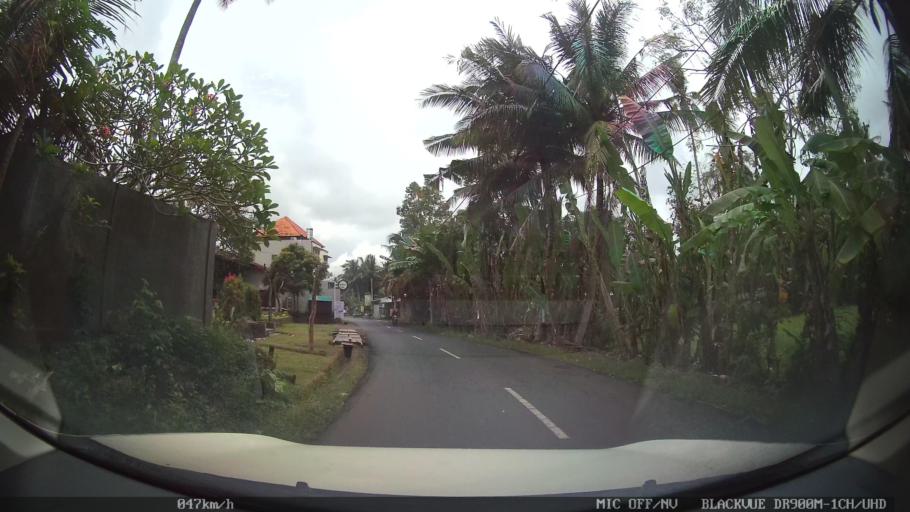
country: ID
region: Bali
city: Banjar Parekan
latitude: -8.5793
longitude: 115.2120
